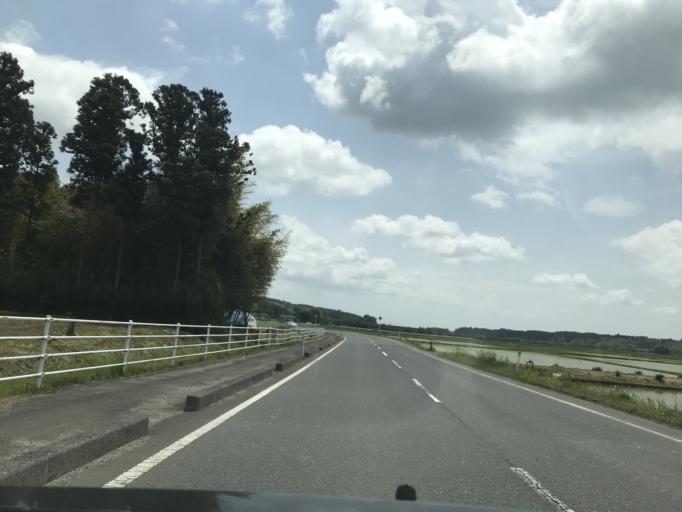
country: JP
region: Miyagi
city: Furukawa
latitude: 38.6812
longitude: 140.9766
